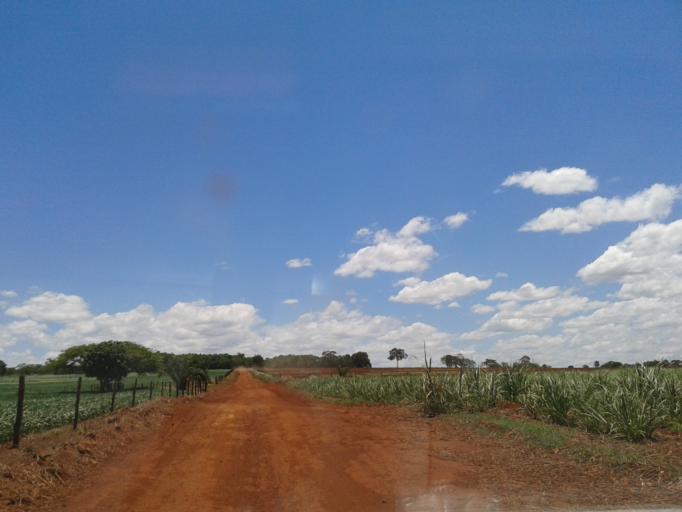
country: BR
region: Minas Gerais
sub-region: Centralina
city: Centralina
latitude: -18.6782
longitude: -49.2276
